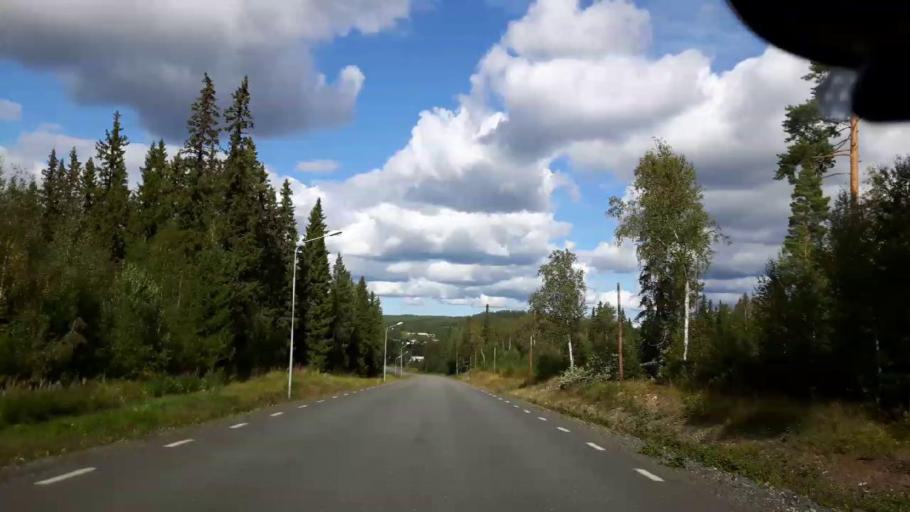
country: SE
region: Jaemtland
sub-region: Braecke Kommun
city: Braecke
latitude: 63.2878
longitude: 15.5872
